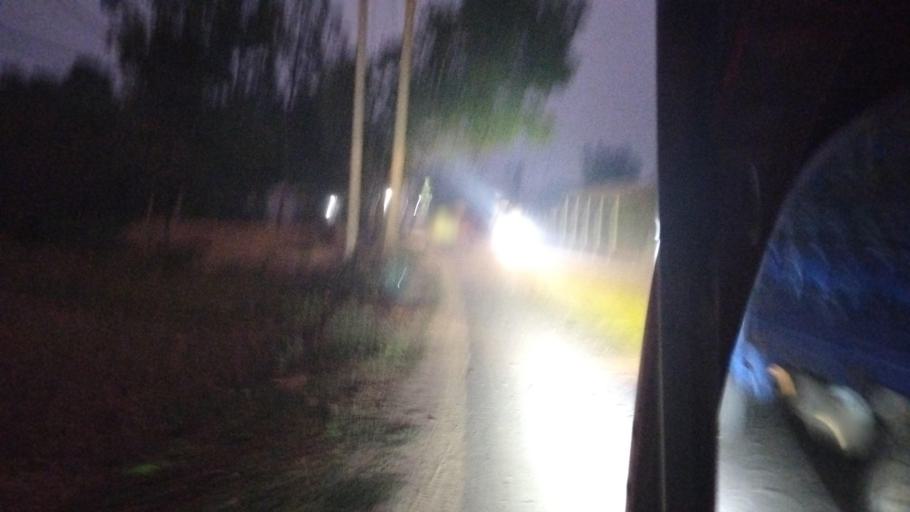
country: BD
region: Dhaka
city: Sakhipur
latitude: 24.3986
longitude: 90.3427
